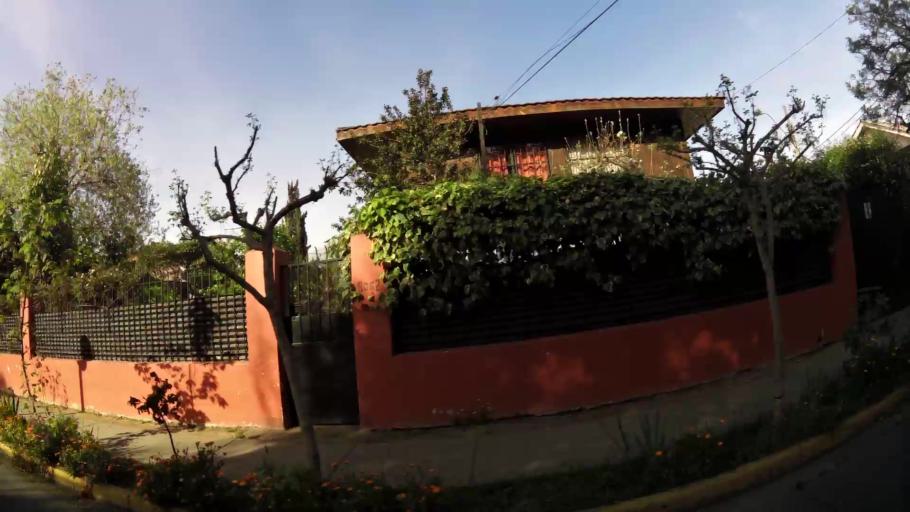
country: CL
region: Santiago Metropolitan
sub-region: Provincia de Santiago
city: Villa Presidente Frei, Nunoa, Santiago, Chile
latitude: -33.5270
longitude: -70.5832
